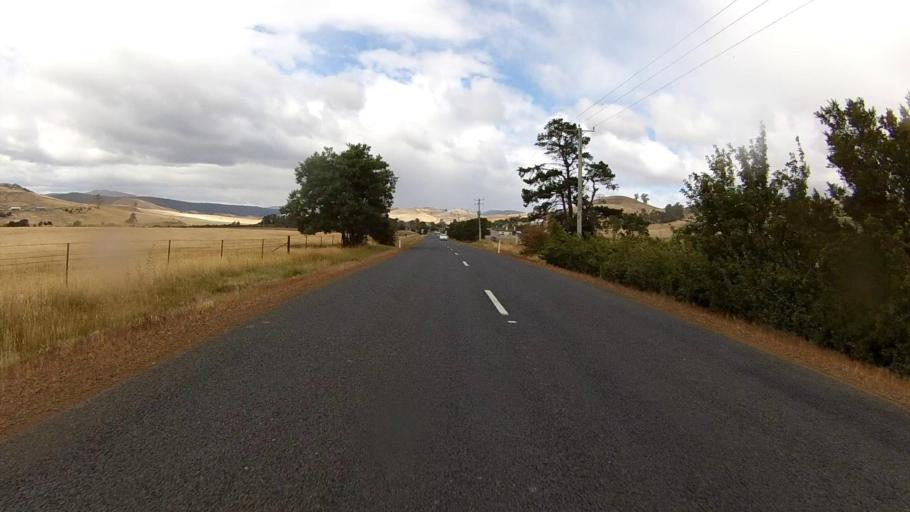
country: AU
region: Tasmania
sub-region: Brighton
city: Bridgewater
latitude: -42.5285
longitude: 147.3599
